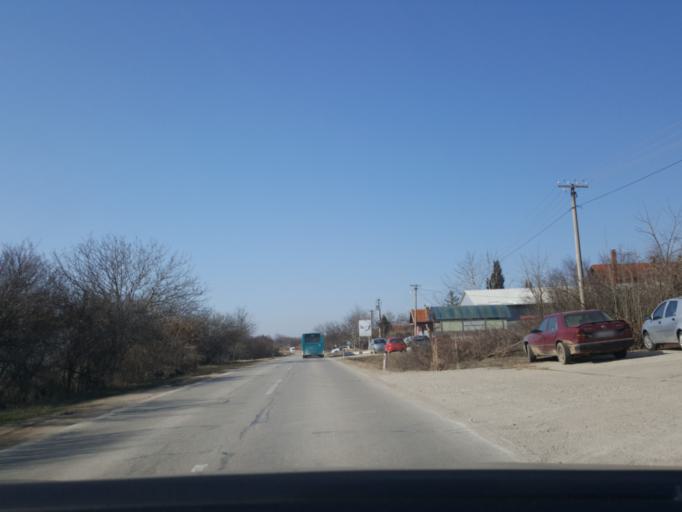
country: RS
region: Central Serbia
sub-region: Nisavski Okrug
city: Nis
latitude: 43.3719
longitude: 21.8321
